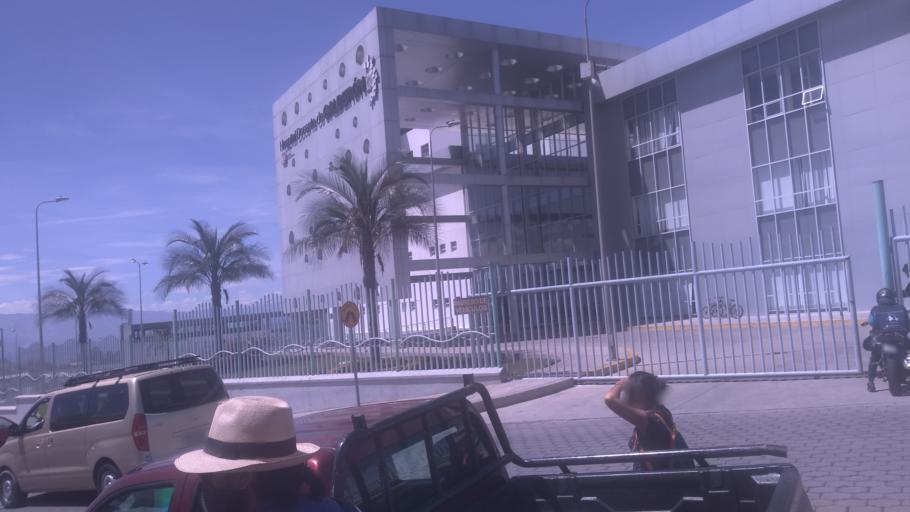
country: EC
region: Pichincha
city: Quito
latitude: -0.0917
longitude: -78.4367
